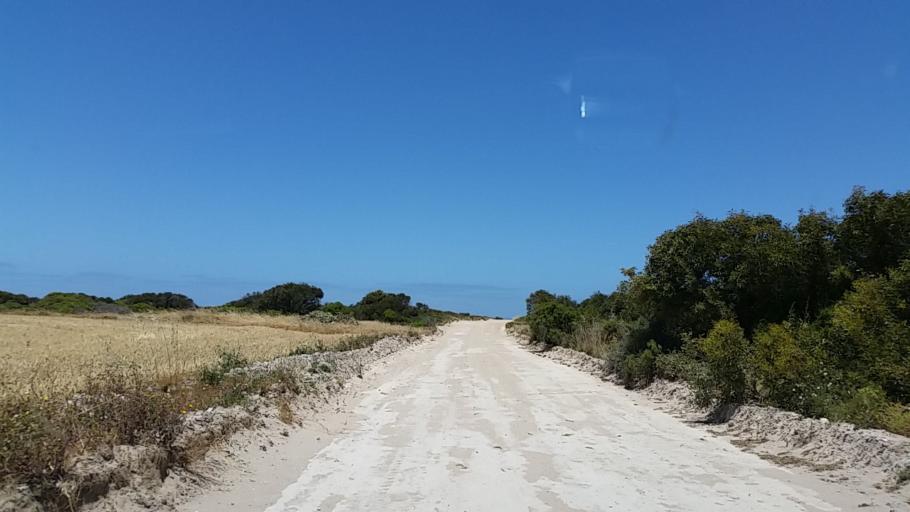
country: AU
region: South Australia
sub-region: Yorke Peninsula
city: Honiton
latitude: -35.2353
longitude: 137.1254
